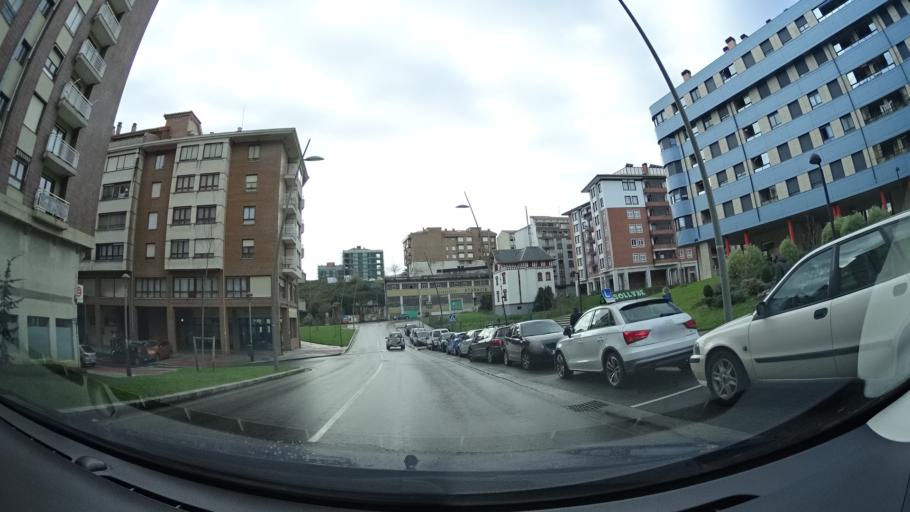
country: ES
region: Basque Country
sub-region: Bizkaia
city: Bermeo
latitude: 43.4207
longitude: -2.7294
